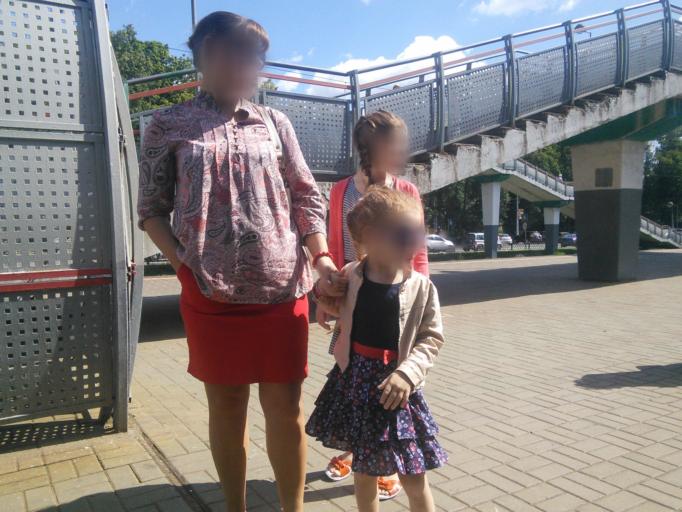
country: RU
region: Moskovskaya
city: Ramenskoye
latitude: 55.5730
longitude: 38.2062
